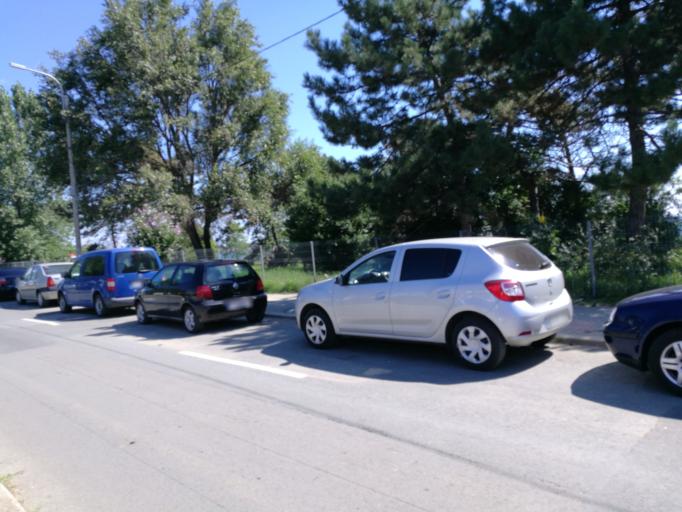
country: RO
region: Constanta
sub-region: Oras Eforie
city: Eforie Nord
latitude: 44.0720
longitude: 28.6377
